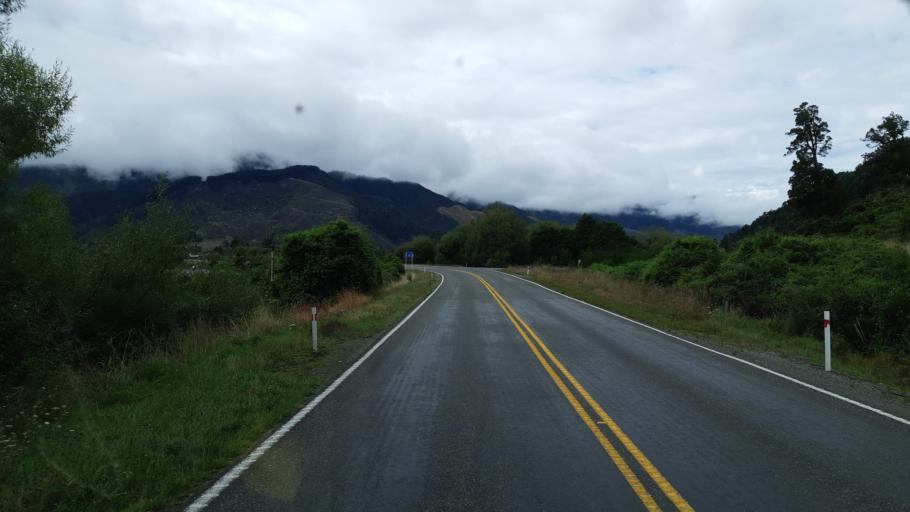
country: NZ
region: West Coast
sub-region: Buller District
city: Westport
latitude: -41.7982
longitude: 172.3127
